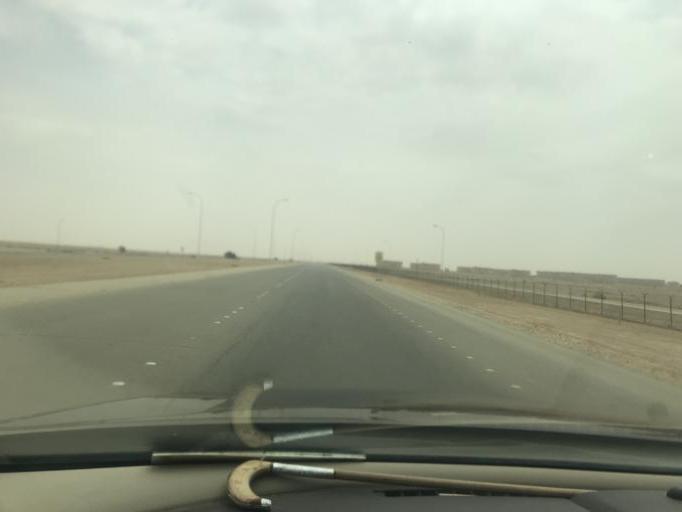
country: SA
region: Ar Riyad
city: Riyadh
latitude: 24.9810
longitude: 46.6651
